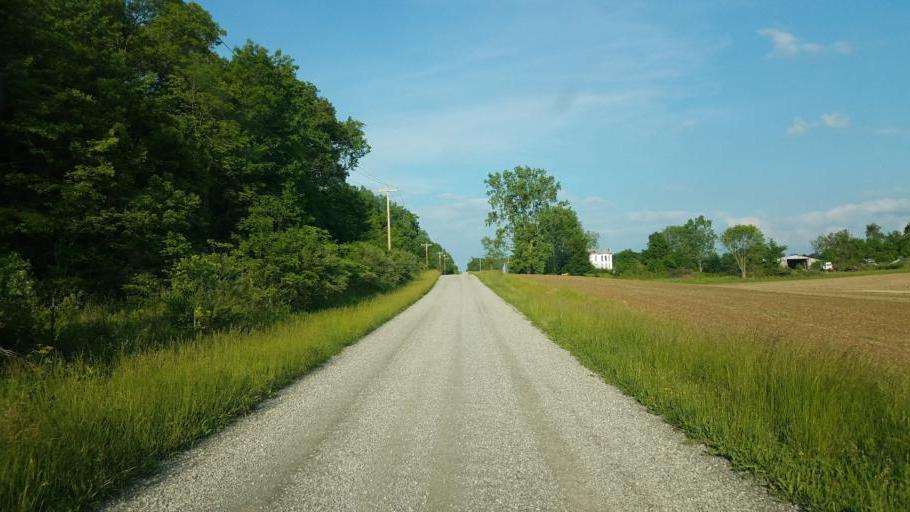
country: US
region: Ohio
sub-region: Morrow County
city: Cardington
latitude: 40.4245
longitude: -82.8039
